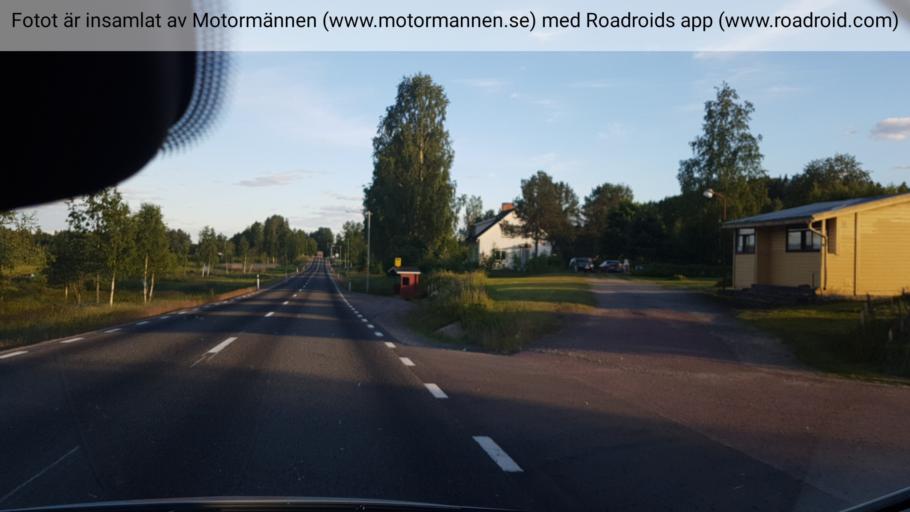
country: SE
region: Vaermland
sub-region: Torsby Kommun
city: Torsby
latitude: 60.2255
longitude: 13.0160
